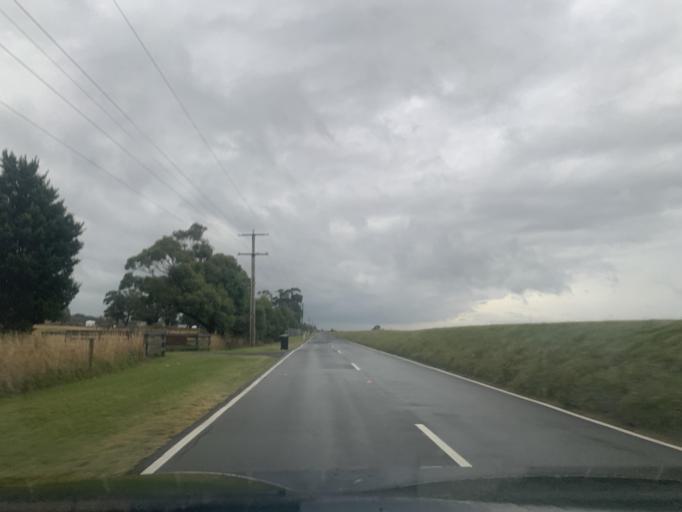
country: AU
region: Victoria
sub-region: Kingston
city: Chelsea Heights
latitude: -38.0268
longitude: 145.1561
